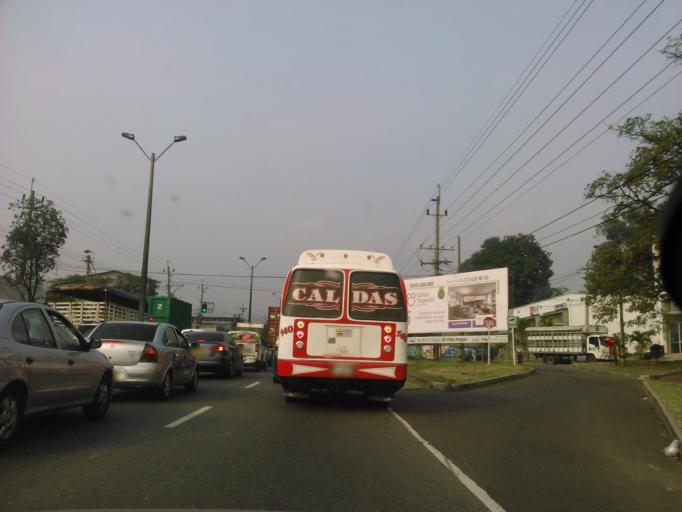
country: CO
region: Antioquia
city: Sabaneta
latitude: 6.1606
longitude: -75.6173
